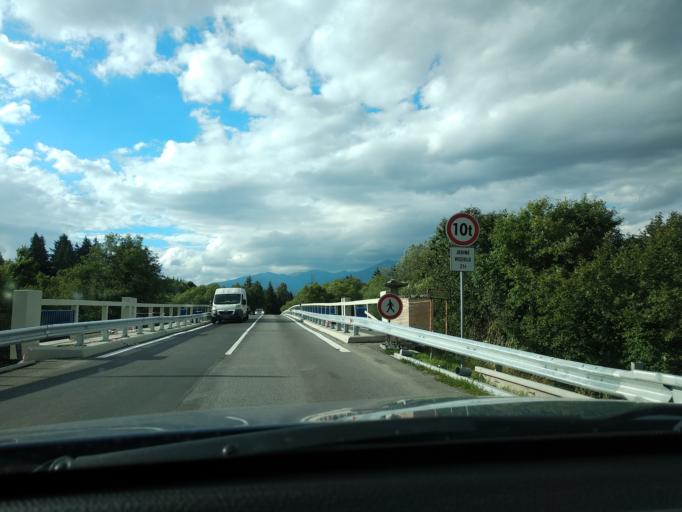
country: SK
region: Zilinsky
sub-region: Okres Zilina
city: Liptovsky Hradok
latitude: 49.0459
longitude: 19.7312
